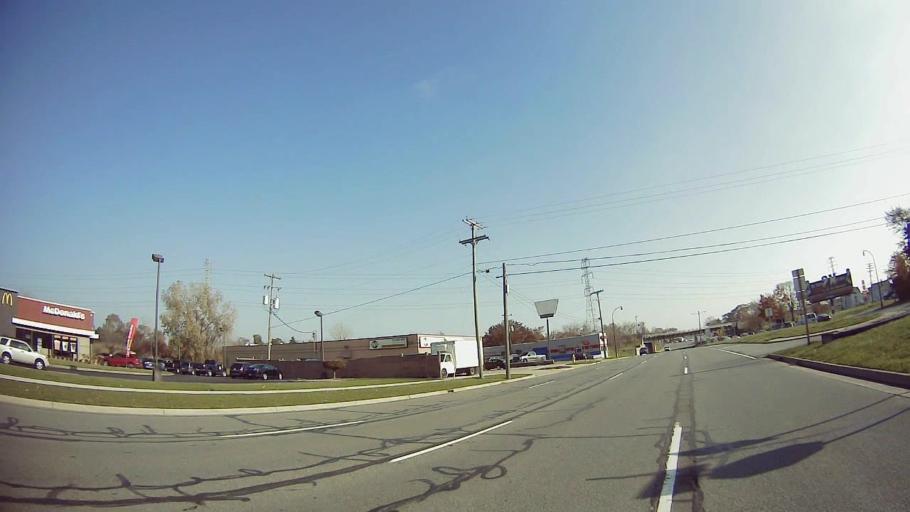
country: US
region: Michigan
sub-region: Wayne County
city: Dearborn
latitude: 42.3297
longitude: -83.1725
